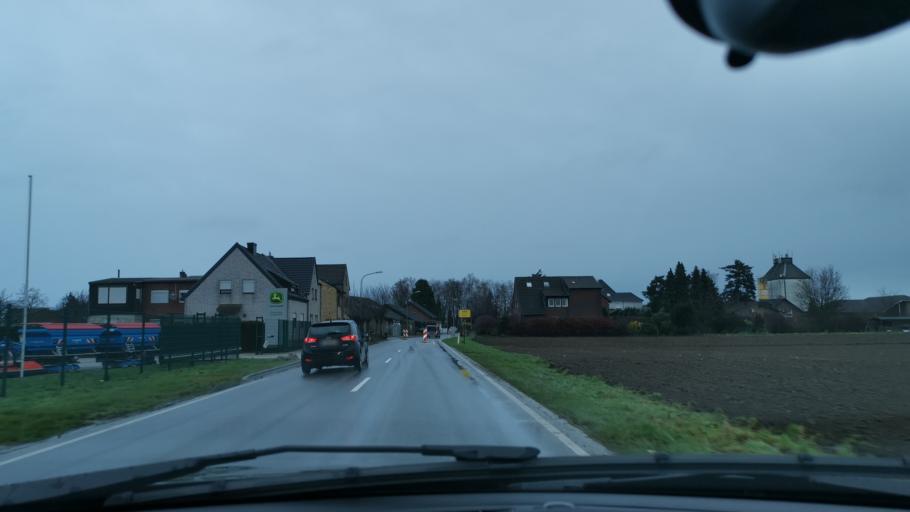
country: DE
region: North Rhine-Westphalia
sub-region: Regierungsbezirk Koln
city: Titz
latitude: 50.9832
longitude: 6.4376
